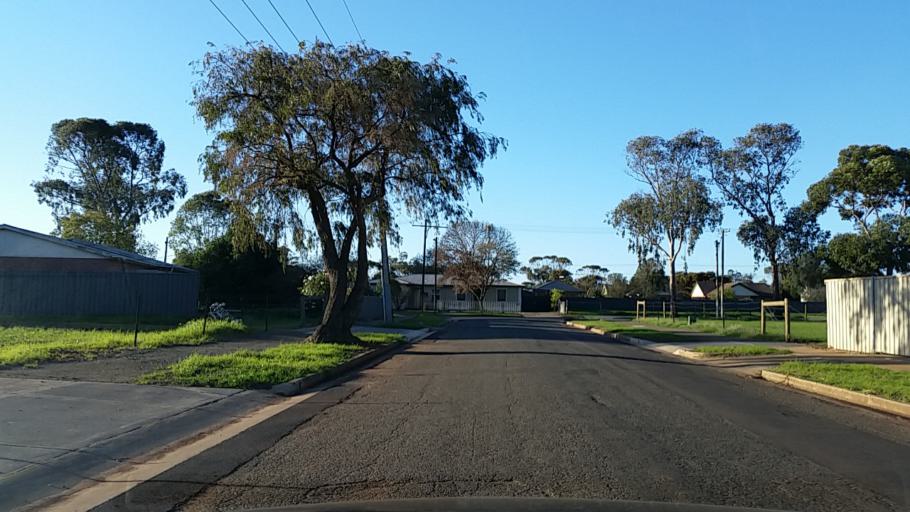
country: AU
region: South Australia
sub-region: Playford
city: Smithfield
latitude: -34.6809
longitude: 138.6688
